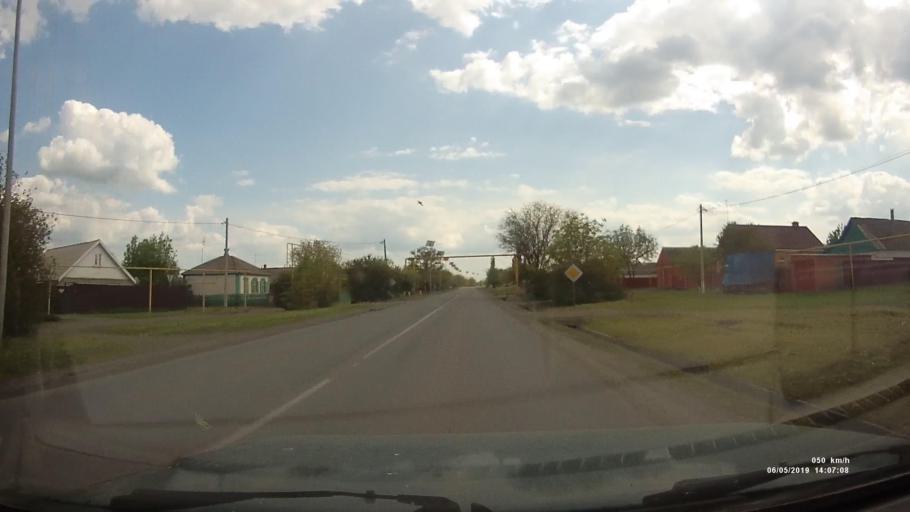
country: RU
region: Rostov
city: Shakhty
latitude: 47.6833
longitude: 40.3030
